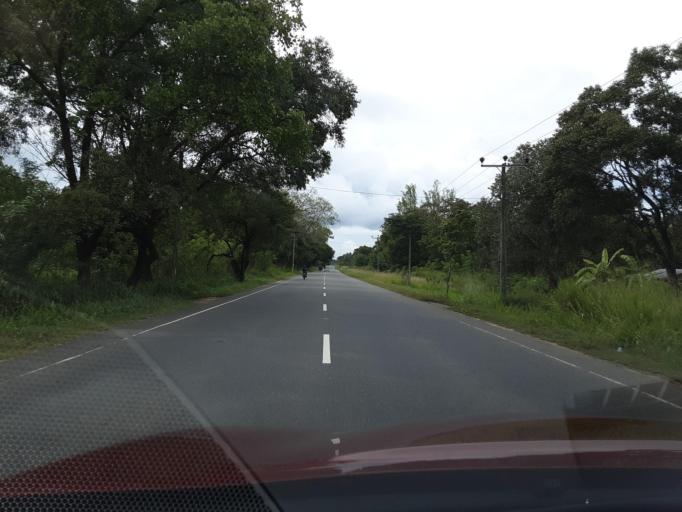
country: LK
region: Uva
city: Badulla
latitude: 7.3916
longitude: 81.1343
